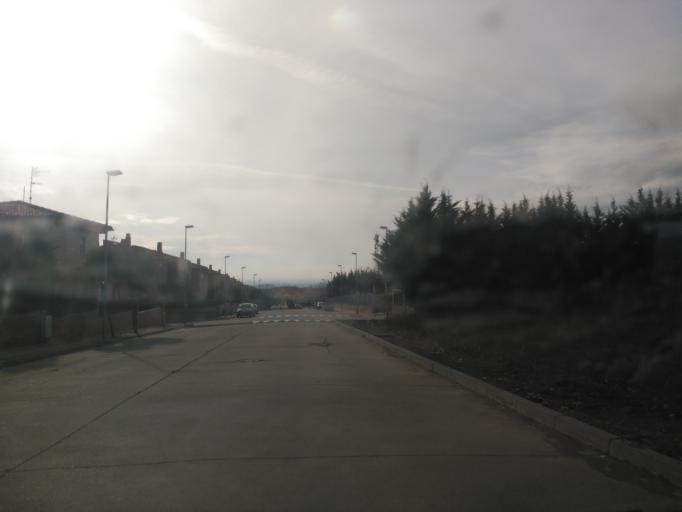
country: ES
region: Castille and Leon
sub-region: Provincia de Salamanca
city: Cabrerizos
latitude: 40.9824
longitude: -5.6059
